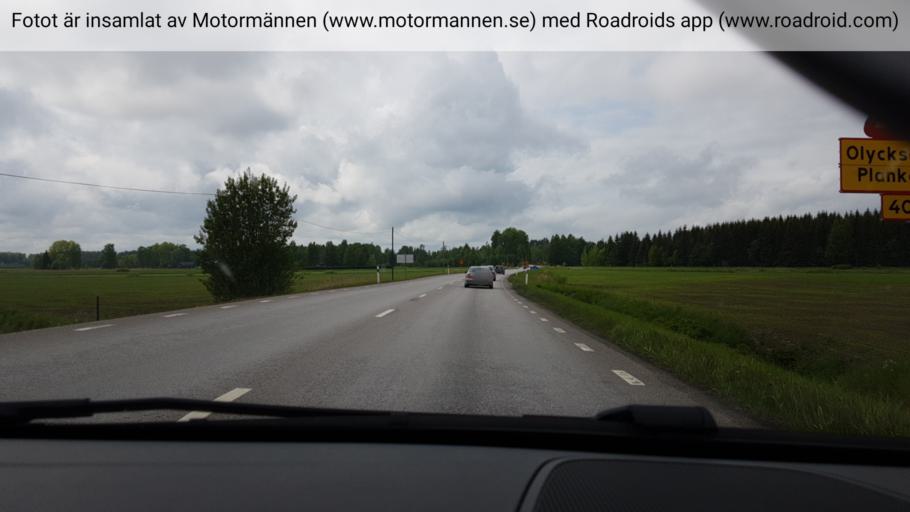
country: SE
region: Uppsala
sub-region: Osthammars Kommun
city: Osterbybruk
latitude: 60.1626
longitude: 17.9837
